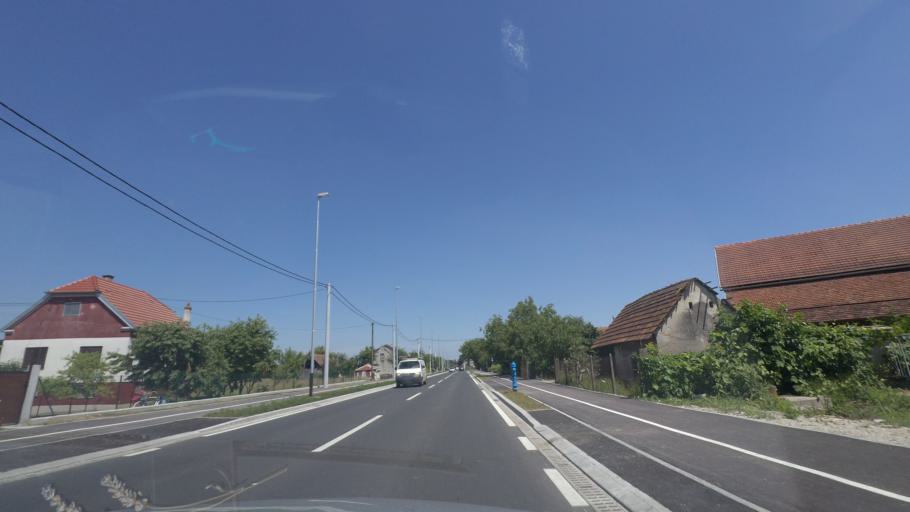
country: HR
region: Grad Zagreb
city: Jezdovec
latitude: 45.7560
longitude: 15.8401
